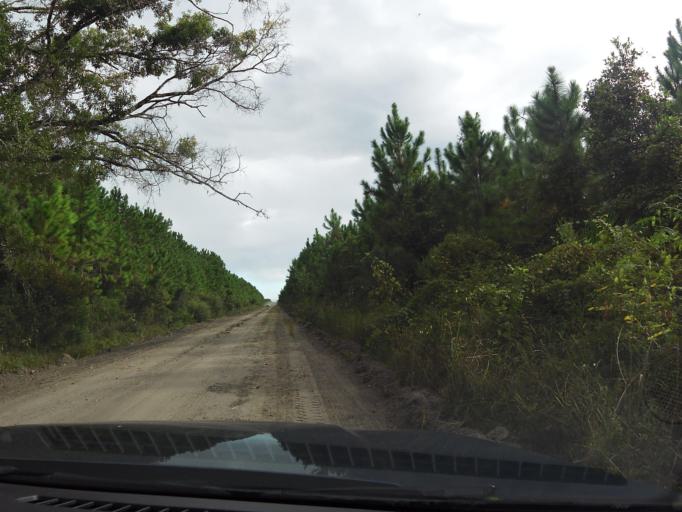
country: US
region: Florida
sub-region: Flagler County
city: Bunnell
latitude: 29.5678
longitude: -81.3367
